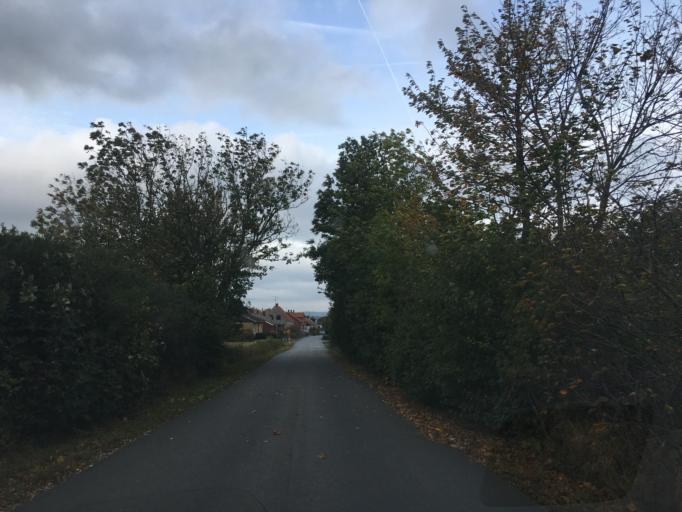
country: SE
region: Skane
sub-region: Simrishamns Kommun
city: Simrishamn
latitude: 55.5896
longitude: 14.3189
